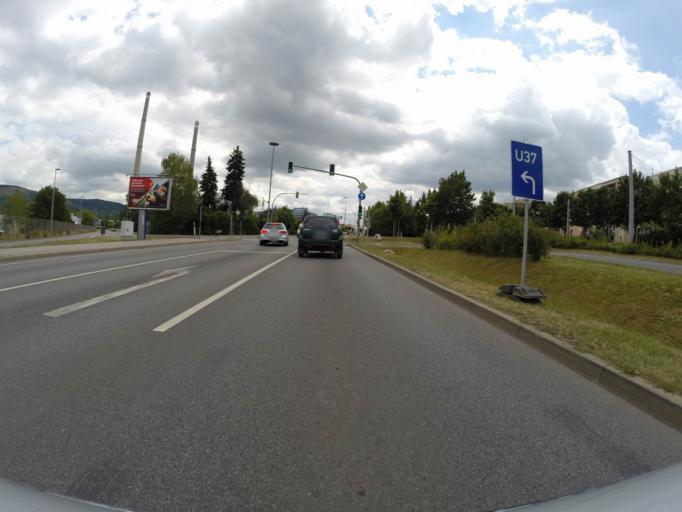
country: DE
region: Thuringia
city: Jena
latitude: 50.8991
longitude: 11.5795
